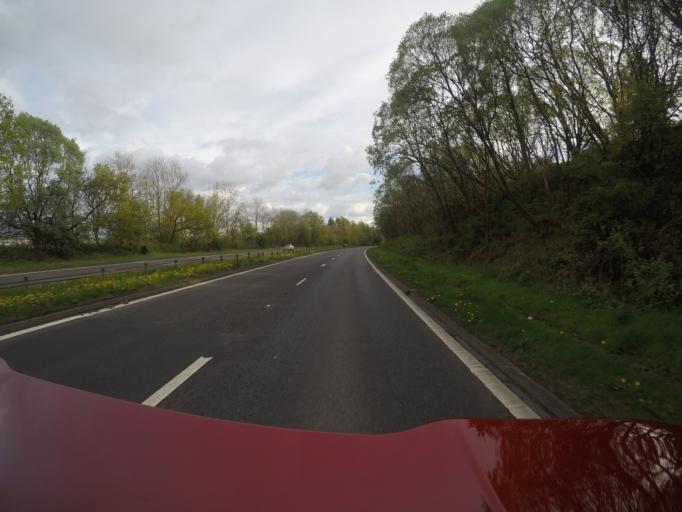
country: GB
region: Scotland
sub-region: West Dunbartonshire
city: Alexandria
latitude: 55.9836
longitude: -4.5871
